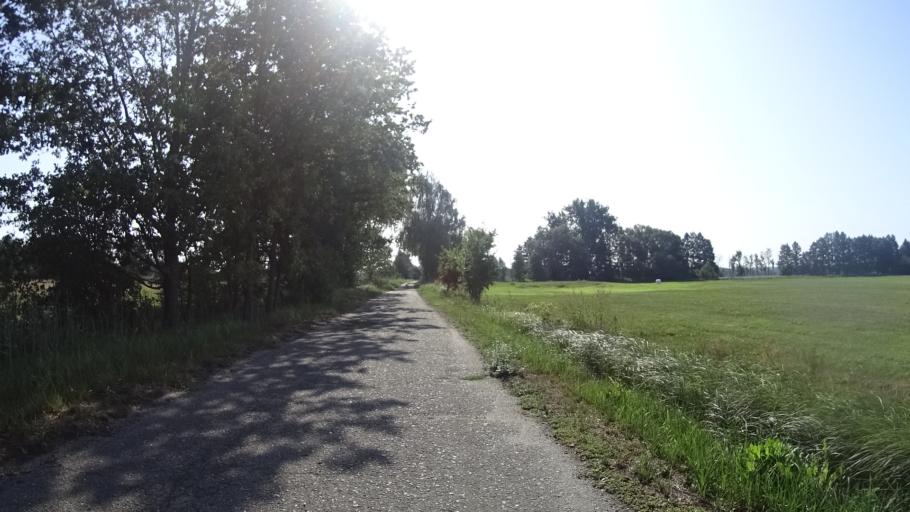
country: DE
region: Brandenburg
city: Neu Zauche
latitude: 51.9092
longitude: 14.0604
